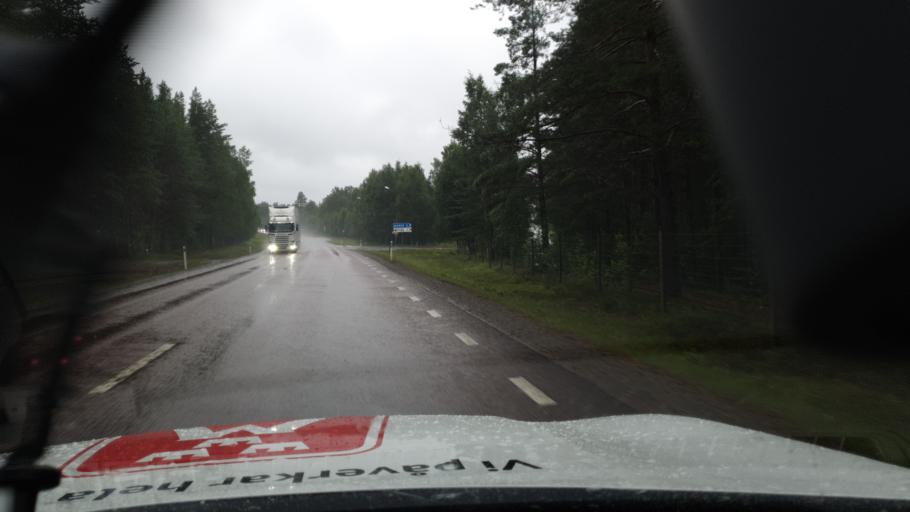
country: SE
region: Vaesterbotten
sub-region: Skelleftea Kommun
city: Burea
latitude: 64.6006
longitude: 21.2043
